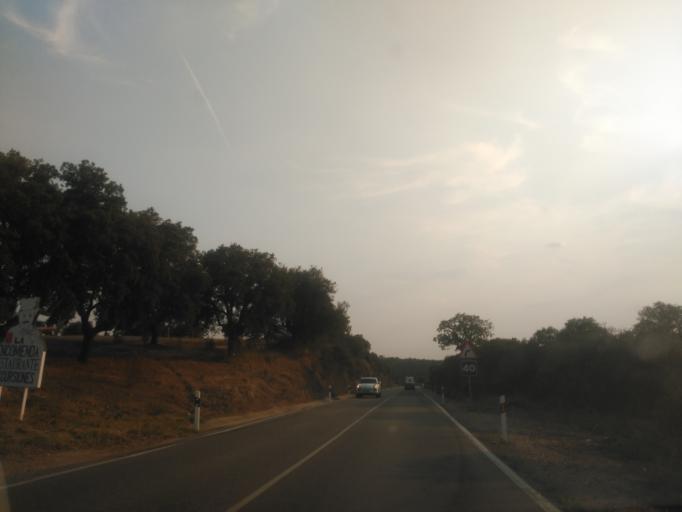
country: ES
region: Castille and Leon
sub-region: Provincia de Zamora
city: San Cebrian de Castro
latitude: 41.7039
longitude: -5.8082
